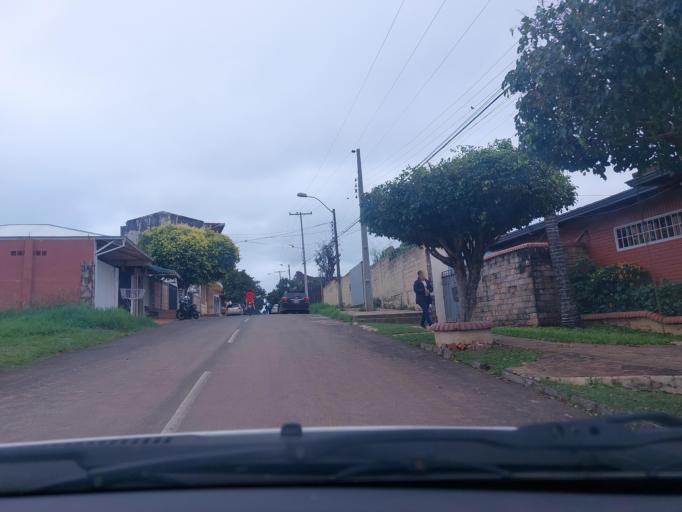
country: PY
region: San Pedro
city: Guayaybi
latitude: -24.6662
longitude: -56.4427
